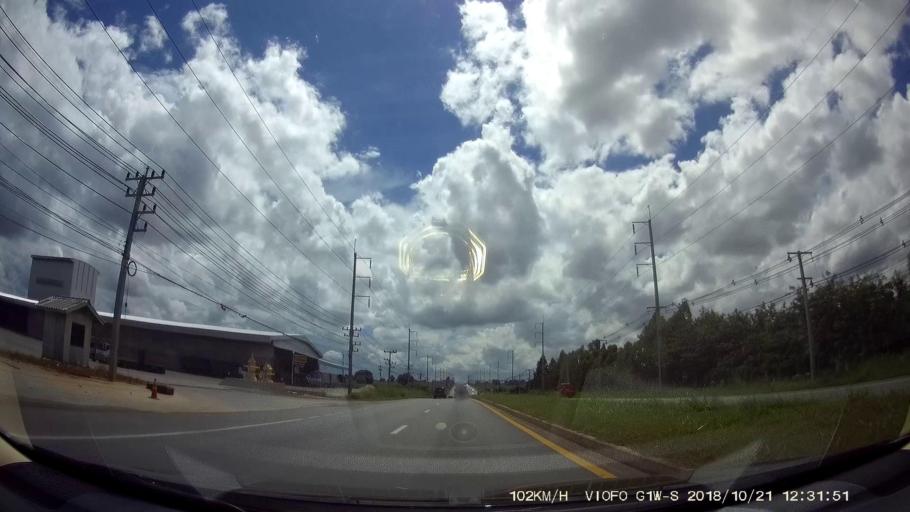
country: TH
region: Nakhon Ratchasima
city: Dan Khun Thot
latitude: 15.1504
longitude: 101.7331
